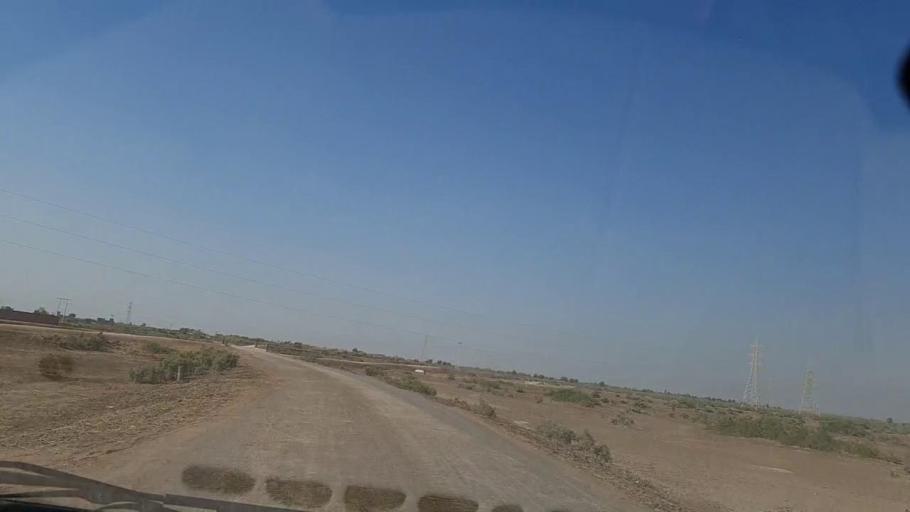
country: PK
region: Sindh
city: Mirpur Khas
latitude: 25.5194
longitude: 68.9486
